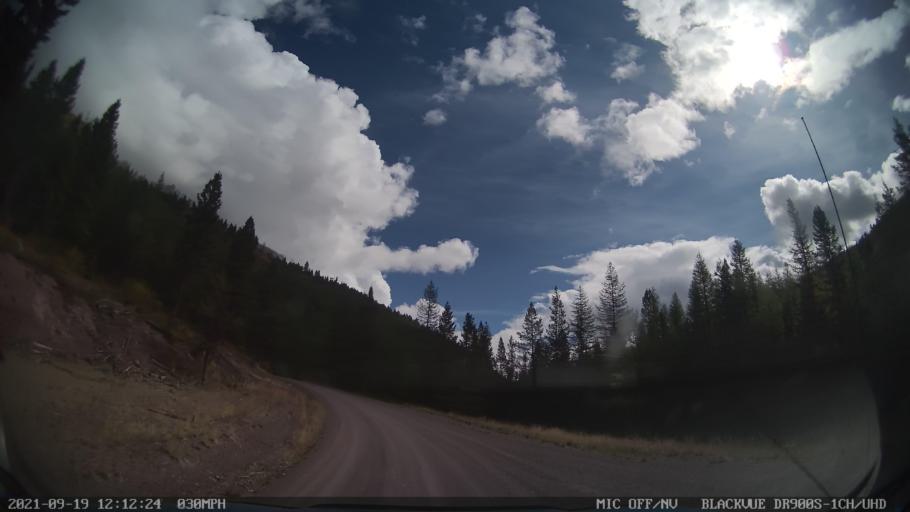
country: US
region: Montana
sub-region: Missoula County
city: Seeley Lake
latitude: 47.1708
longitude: -113.3662
